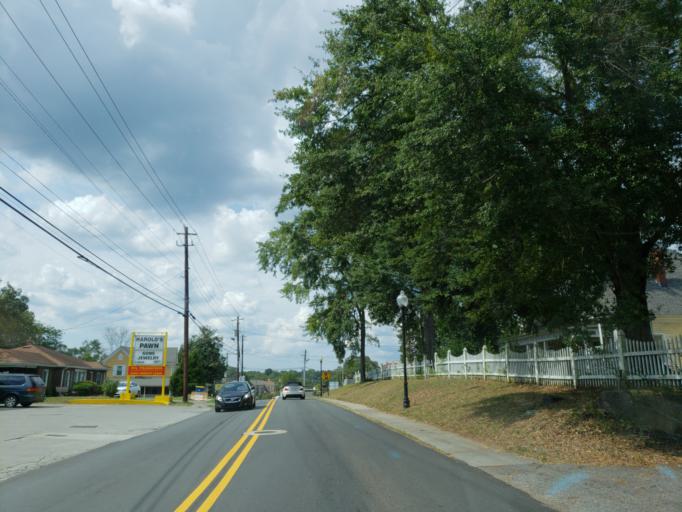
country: US
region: Georgia
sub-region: Cobb County
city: Kennesaw
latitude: 34.0182
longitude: -84.6132
